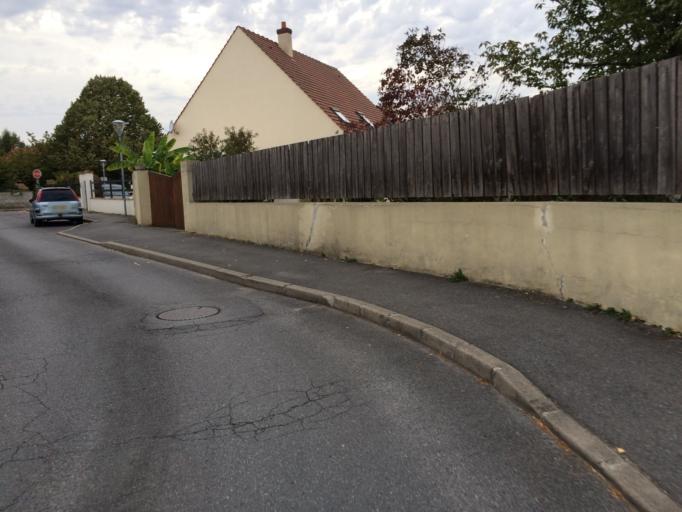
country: FR
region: Ile-de-France
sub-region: Departement de l'Essonne
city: Marcoussis
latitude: 48.6408
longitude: 2.2285
